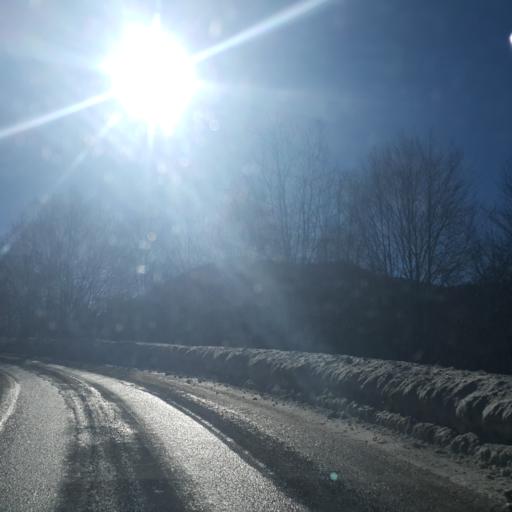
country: XK
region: Mitrovica
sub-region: Komuna e Leposaviqit
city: Leposaviq
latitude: 43.3100
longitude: 20.8605
